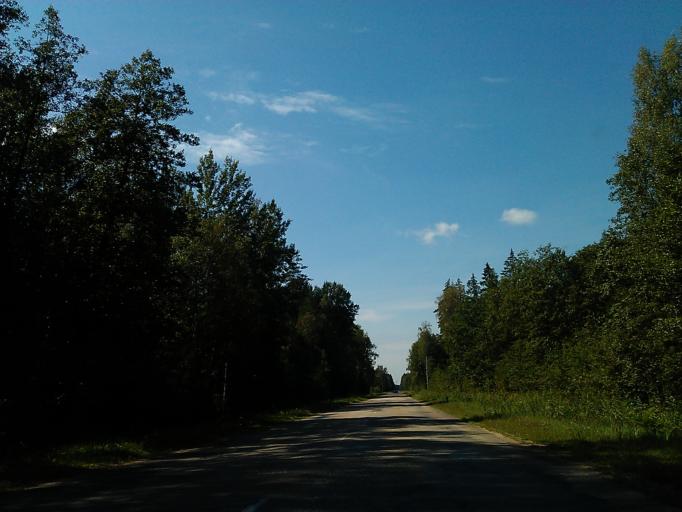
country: LV
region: Garkalne
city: Garkalne
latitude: 56.9454
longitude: 24.4539
